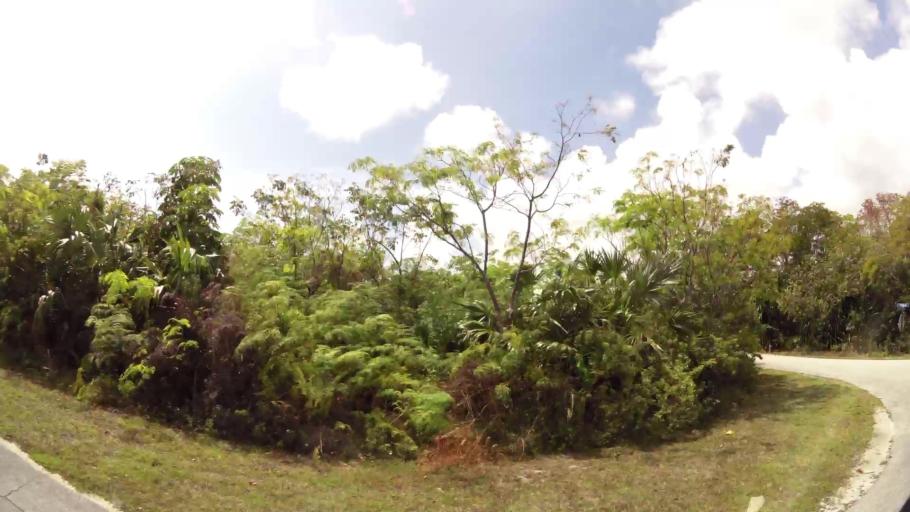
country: BS
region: Freeport
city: Freeport
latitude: 26.5113
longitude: -78.7092
